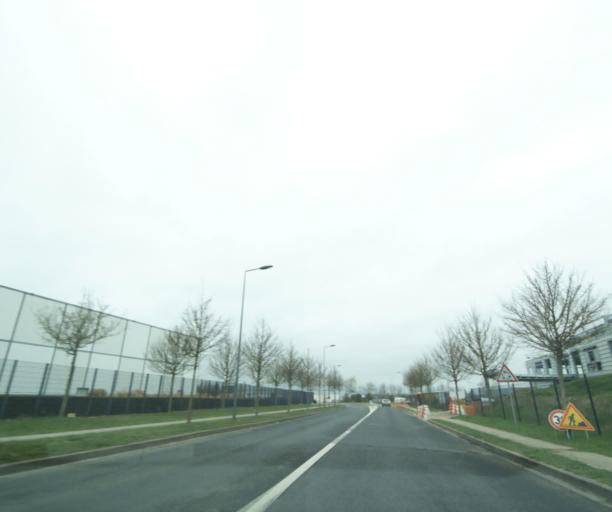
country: FR
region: Ile-de-France
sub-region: Departement du Val-d'Oise
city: Vaureal
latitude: 49.0557
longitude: 2.0326
